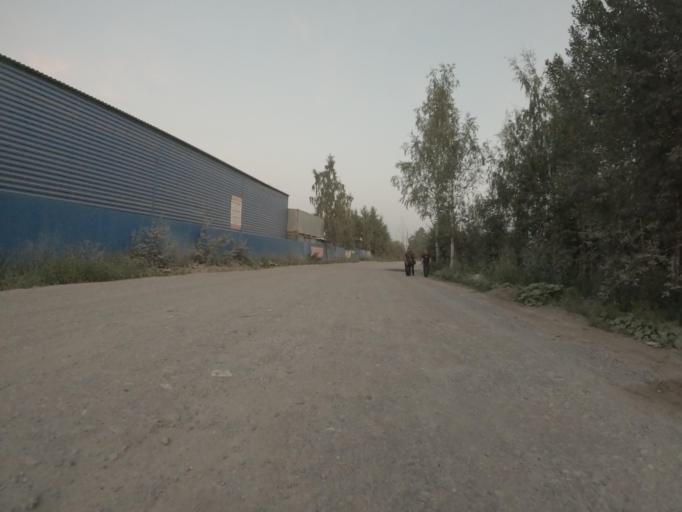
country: RU
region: Leningrad
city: Yanino Vtoroye
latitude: 59.9398
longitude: 30.6012
